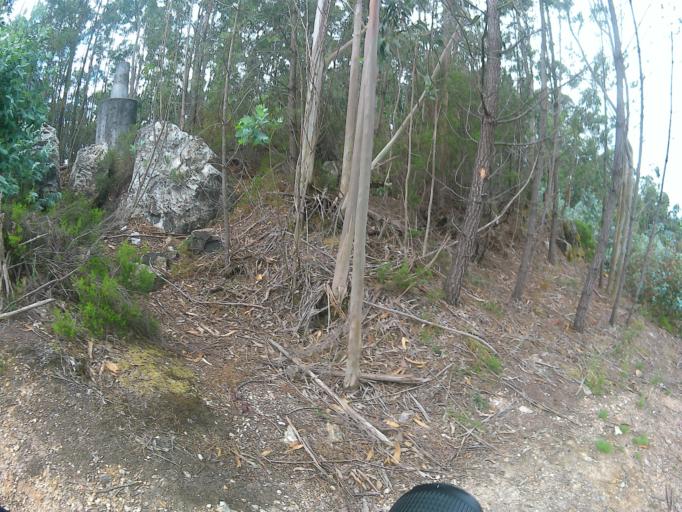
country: PT
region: Aveiro
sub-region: Albergaria-A-Velha
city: Branca
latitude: 40.7592
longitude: -8.4339
